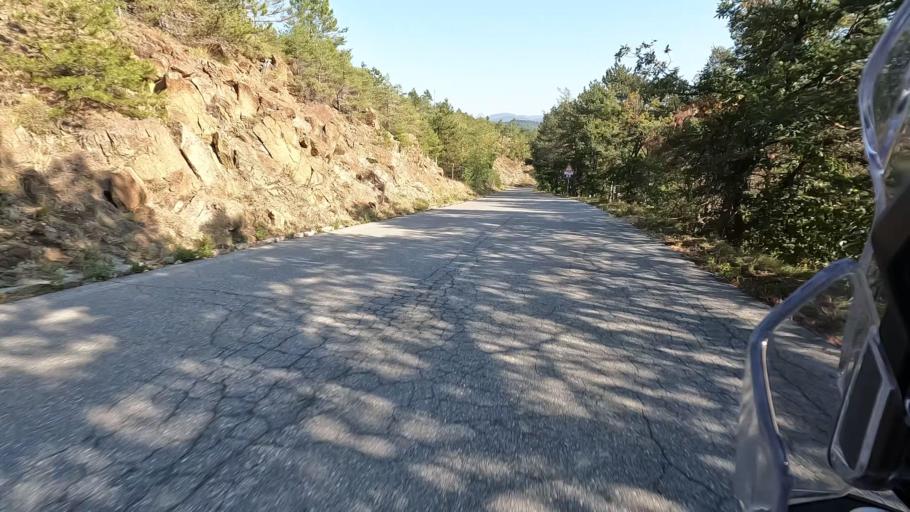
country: IT
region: Liguria
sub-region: Provincia di Savona
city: Urbe
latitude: 44.5030
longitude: 8.5408
